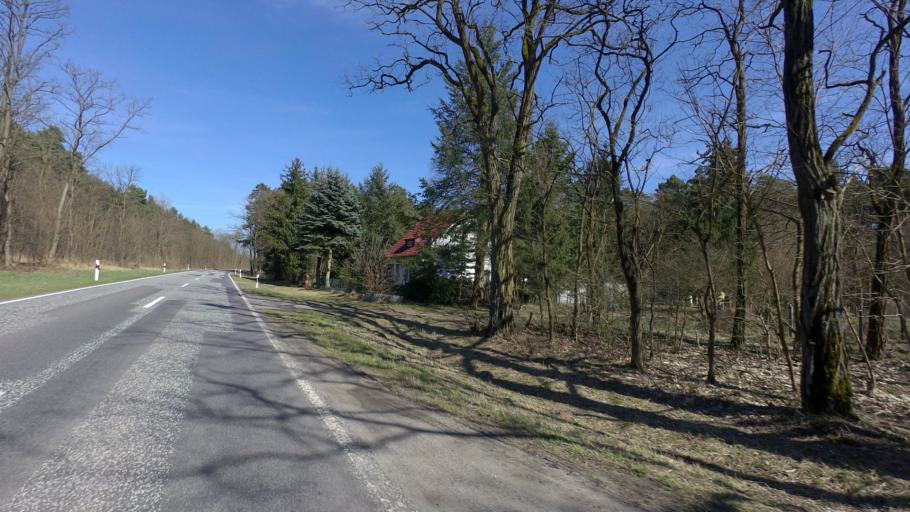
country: DE
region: Brandenburg
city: Muncheberg
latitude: 52.4875
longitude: 14.0811
